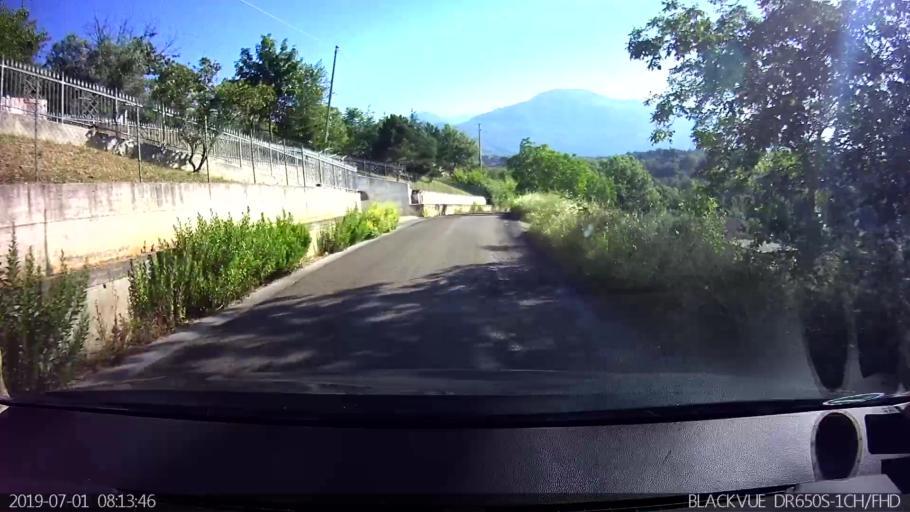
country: IT
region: Latium
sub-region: Provincia di Frosinone
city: Veroli
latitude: 41.6918
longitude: 13.4244
